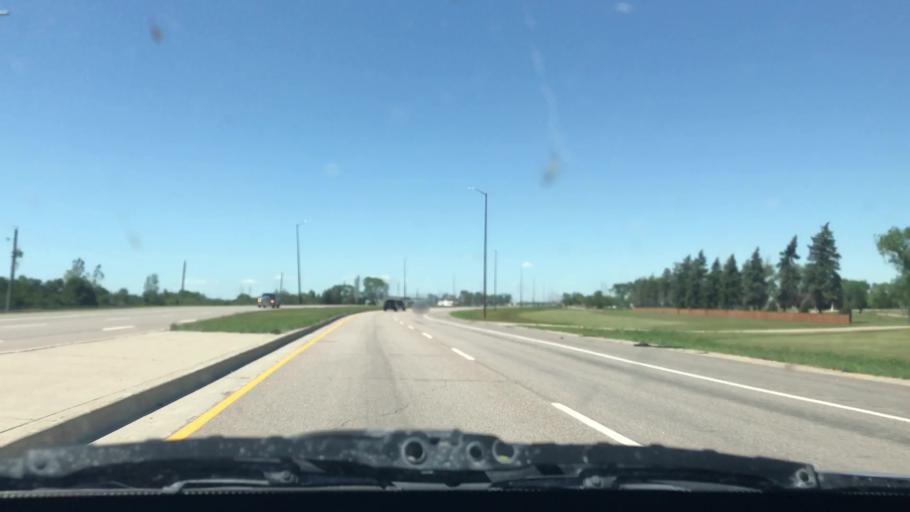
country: CA
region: Manitoba
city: Winnipeg
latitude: 49.8417
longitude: -96.9880
